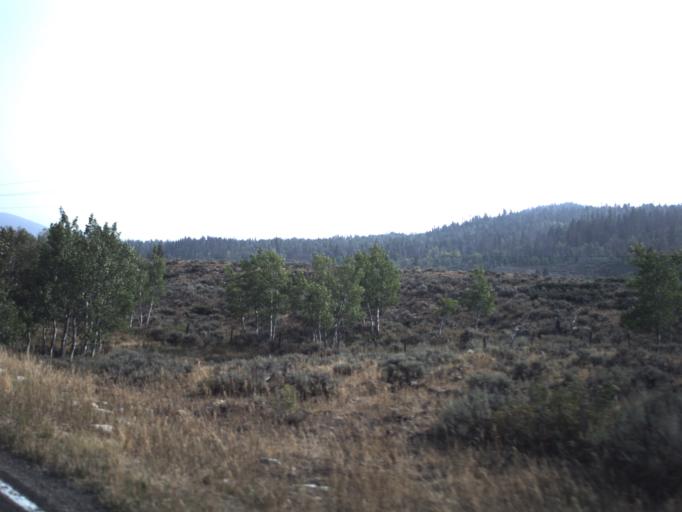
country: US
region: Wyoming
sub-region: Uinta County
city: Evanston
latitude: 40.9341
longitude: -110.8342
